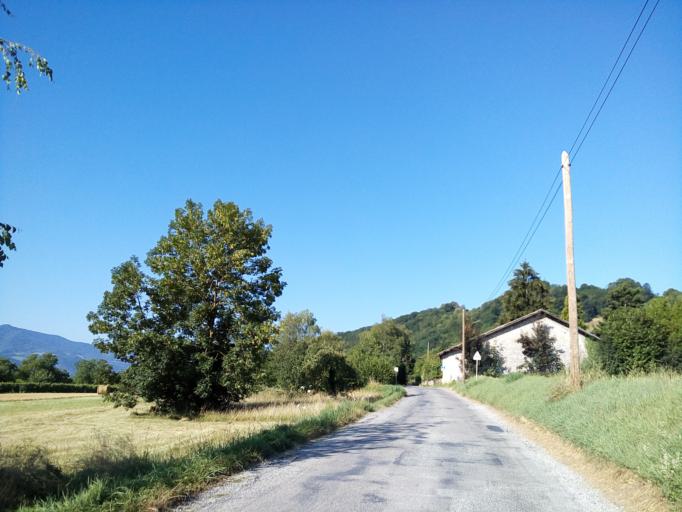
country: FR
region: Rhone-Alpes
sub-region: Departement de l'Isere
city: Bernin
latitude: 45.2612
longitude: 5.8716
